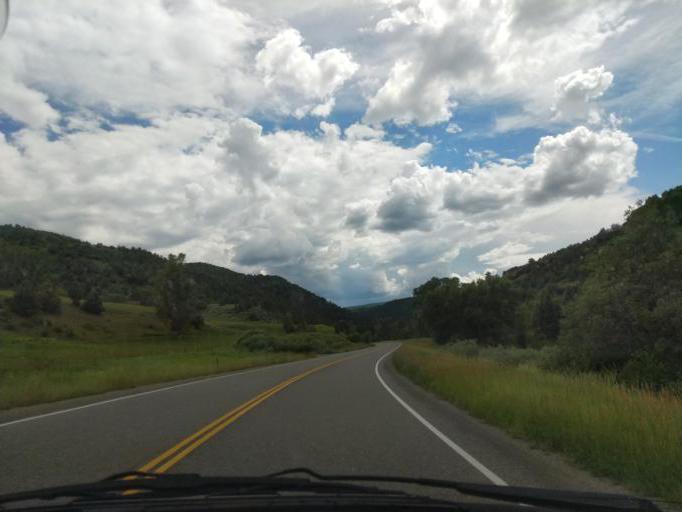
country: US
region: Colorado
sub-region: Delta County
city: Paonia
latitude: 39.0452
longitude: -107.3601
